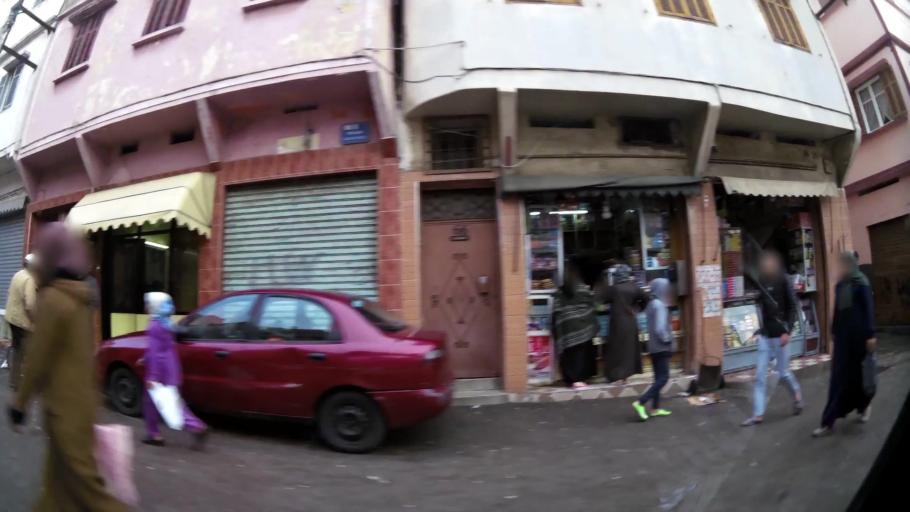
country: MA
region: Grand Casablanca
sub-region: Casablanca
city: Casablanca
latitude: 33.5504
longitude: -7.5783
